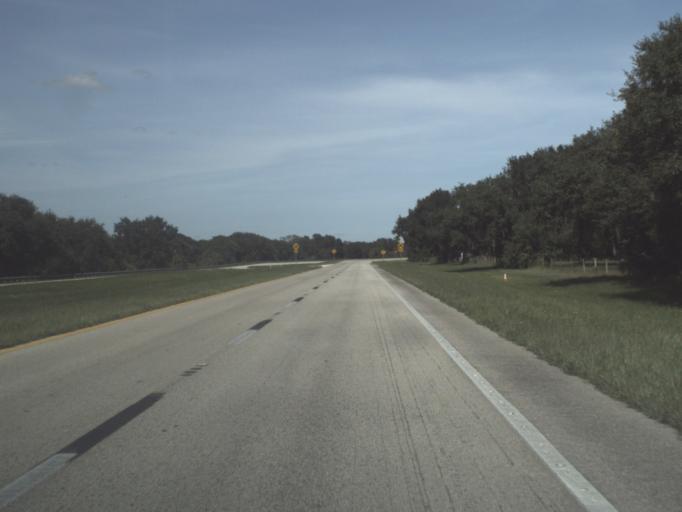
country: US
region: Florida
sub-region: Glades County
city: Moore Haven
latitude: 26.8912
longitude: -81.2355
